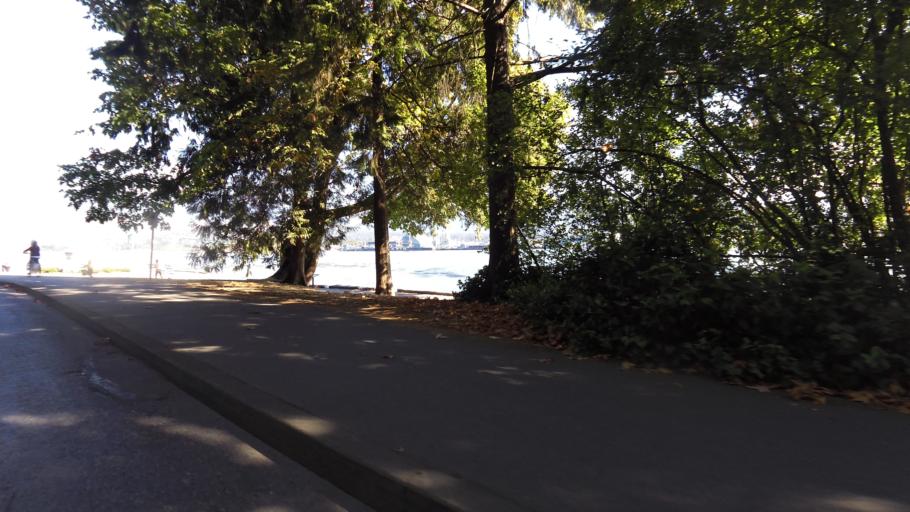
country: CA
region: British Columbia
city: West End
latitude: 49.3022
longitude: -123.1261
